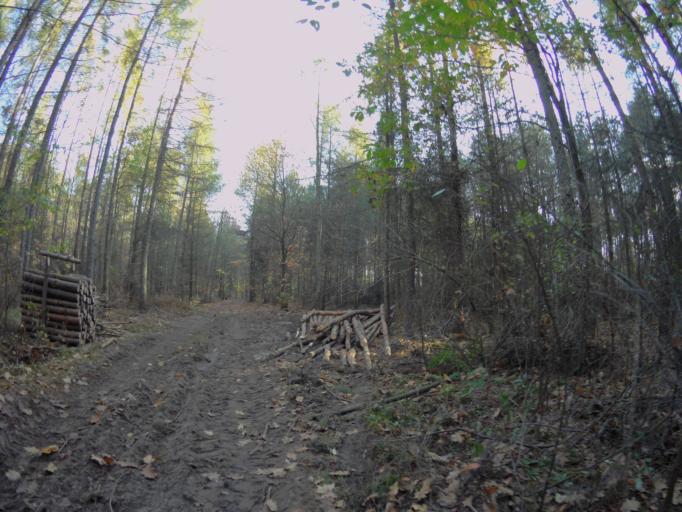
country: PL
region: Subcarpathian Voivodeship
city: Nowa Sarzyna
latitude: 50.3066
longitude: 22.3534
